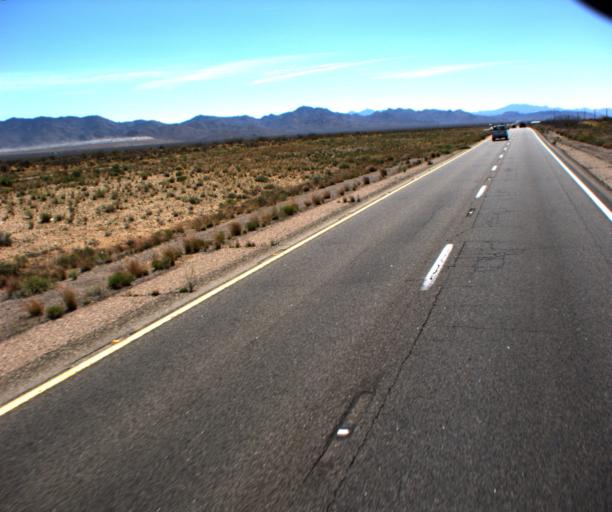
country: US
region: Arizona
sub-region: Mohave County
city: Golden Valley
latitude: 35.3591
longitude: -114.2323
